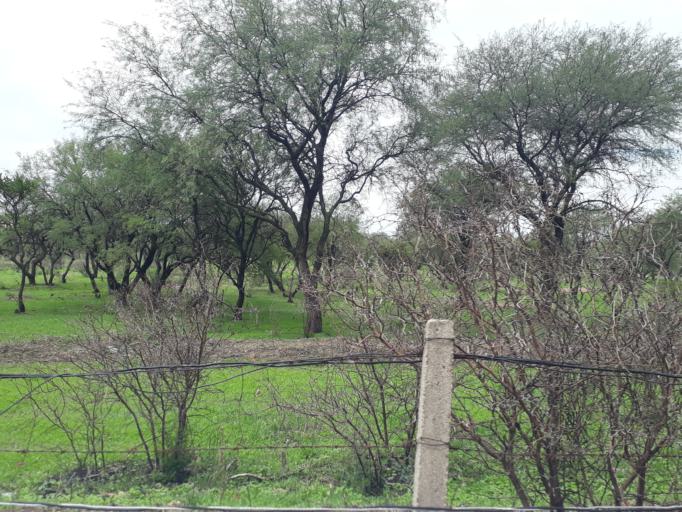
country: MX
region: Aguascalientes
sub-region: Aguascalientes
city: La Loma de los Negritos
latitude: 21.8310
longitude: -102.3251
